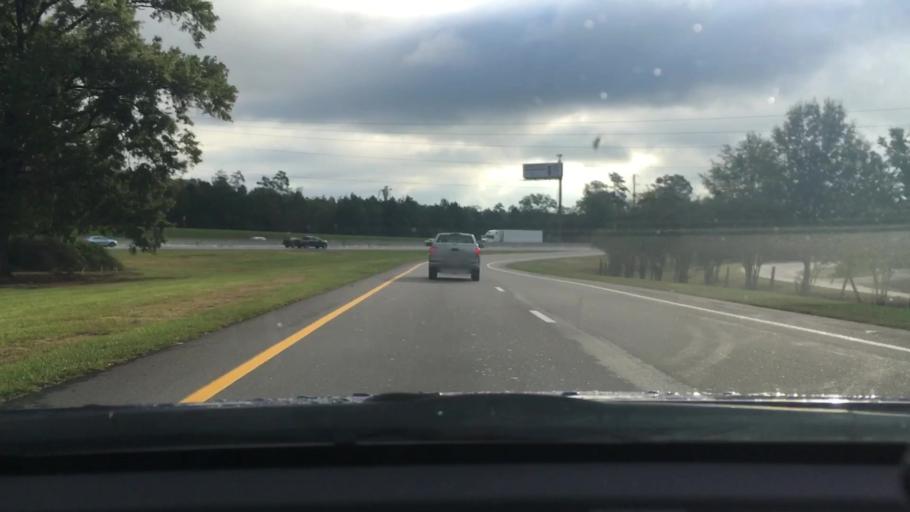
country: US
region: South Carolina
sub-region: Lexington County
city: Irmo
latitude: 34.0975
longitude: -81.1750
